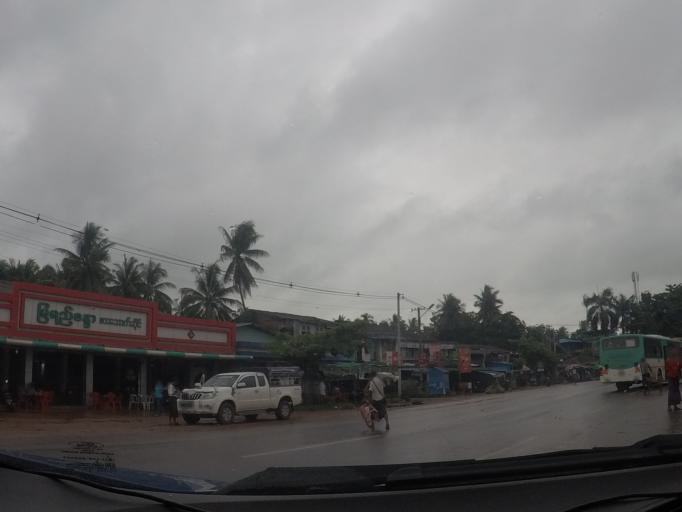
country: MM
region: Bago
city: Letpandan
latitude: 17.7888
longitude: 95.7733
